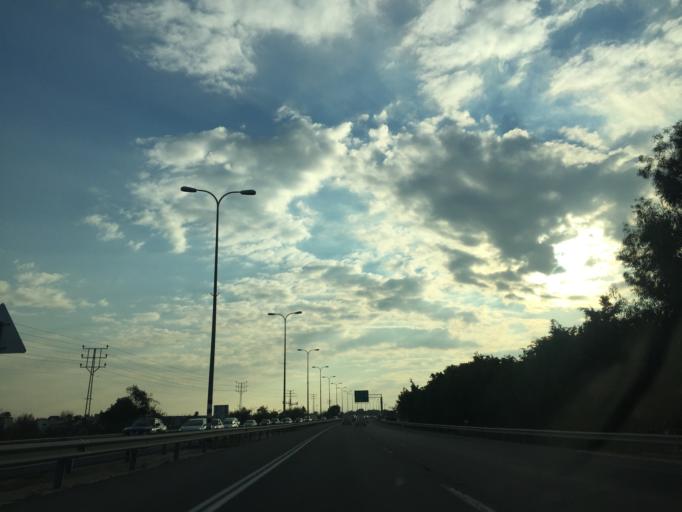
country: IL
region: Central District
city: Lod
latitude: 31.9316
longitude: 34.8906
